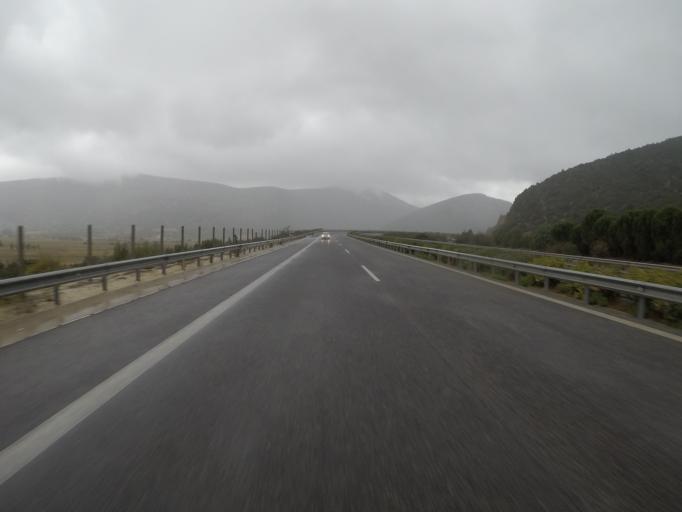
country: GR
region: Peloponnese
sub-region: Nomos Arkadias
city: Tripoli
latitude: 37.6350
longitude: 22.4645
